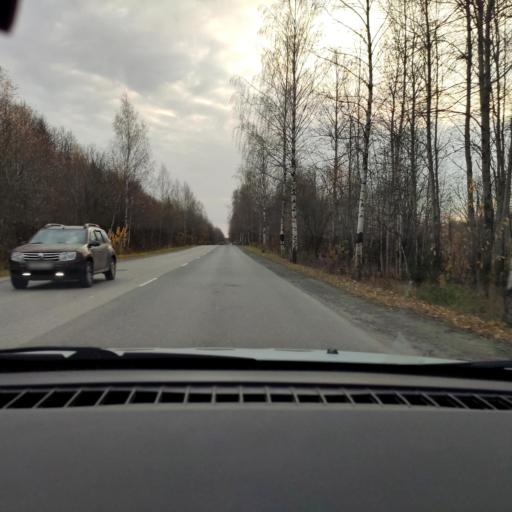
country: RU
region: Perm
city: Perm
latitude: 58.1015
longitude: 56.4119
